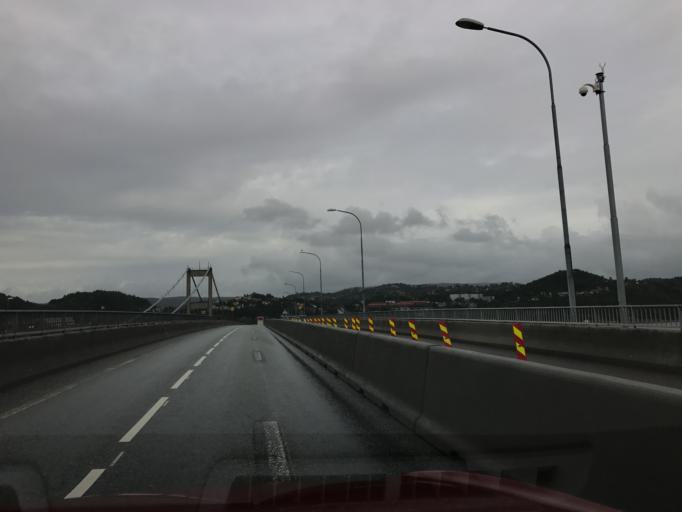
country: NO
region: Vest-Agder
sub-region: Kristiansand
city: Justvik
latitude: 58.1612
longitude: 8.0584
